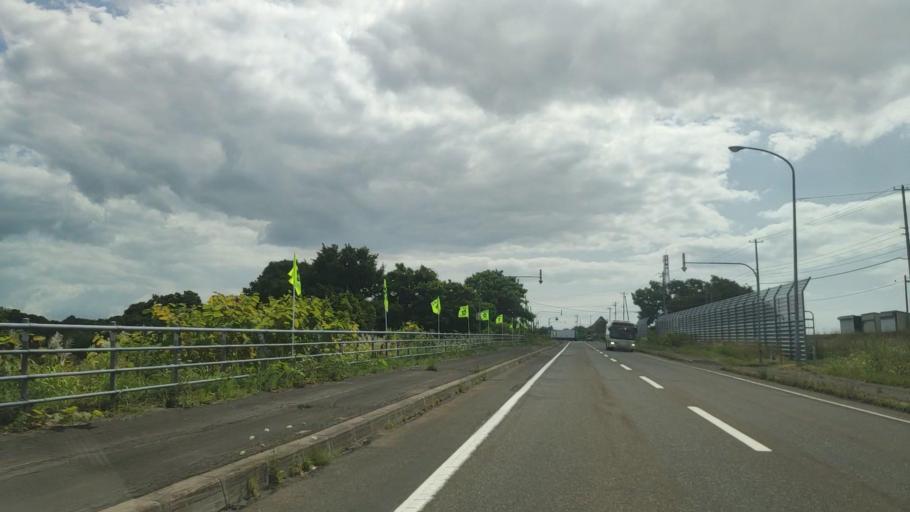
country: JP
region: Hokkaido
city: Rumoi
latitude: 44.5672
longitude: 141.7867
